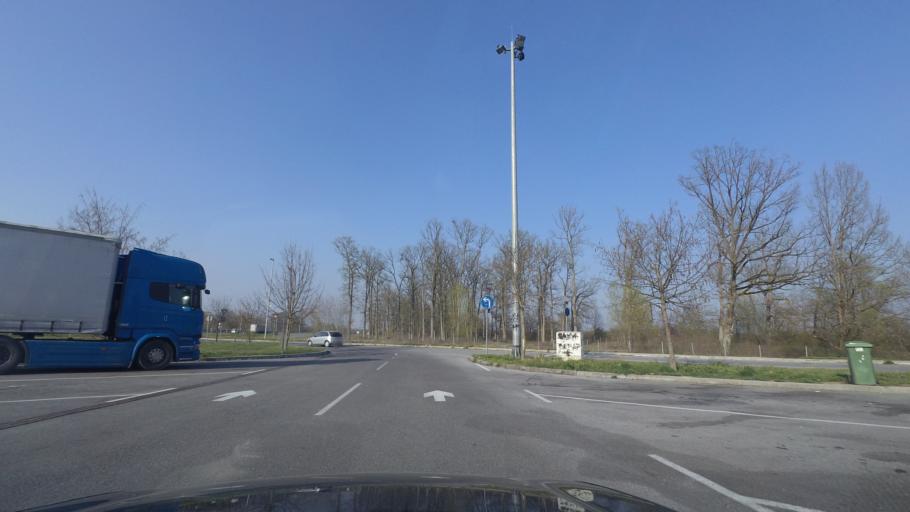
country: HR
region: Karlovacka
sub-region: Grad Karlovac
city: Karlovac
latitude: 45.5590
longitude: 15.6088
